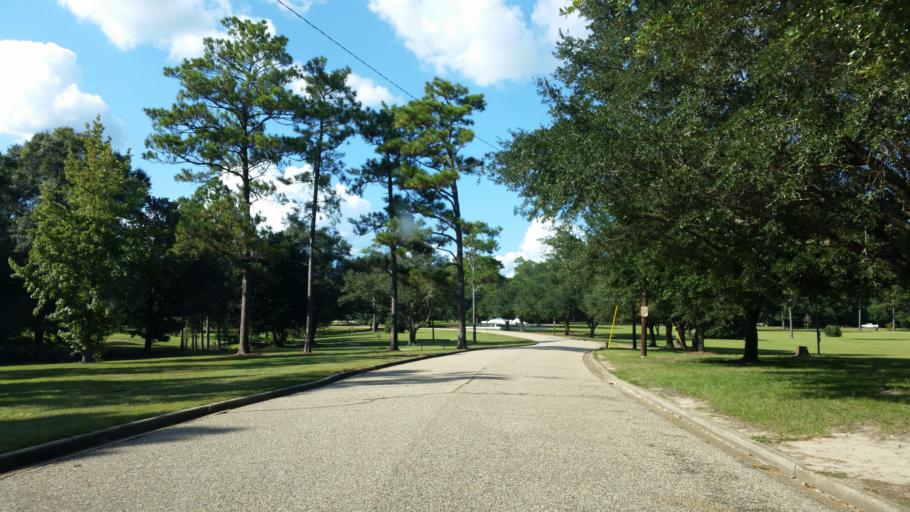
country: US
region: Alabama
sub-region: Mobile County
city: Prichard
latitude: 30.7077
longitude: -88.1615
